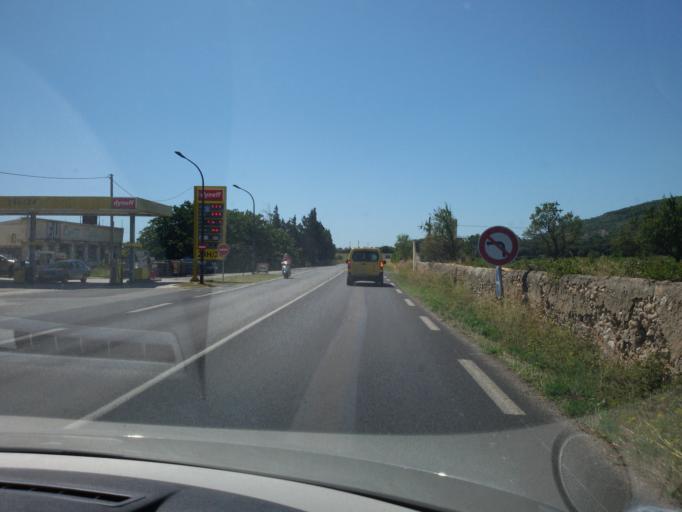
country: FR
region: Languedoc-Roussillon
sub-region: Departement de l'Herault
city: Frontignan
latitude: 43.4715
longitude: 3.7683
